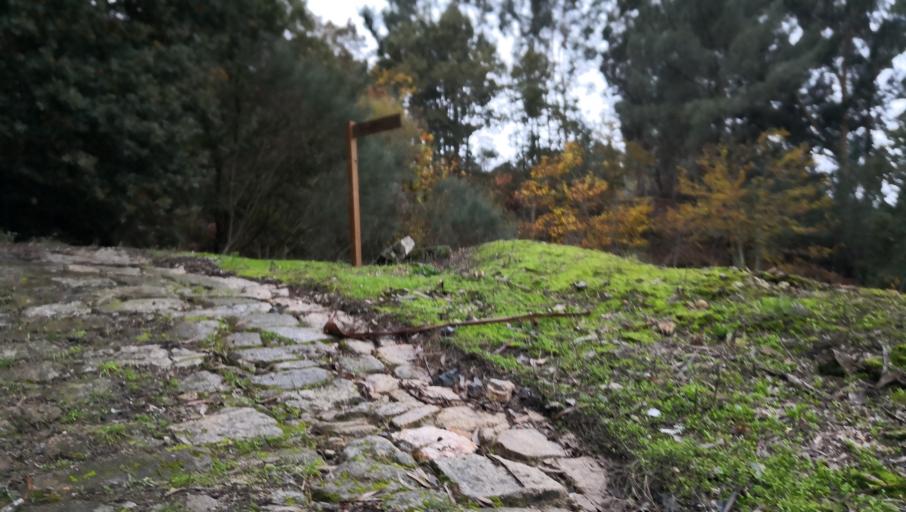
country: PT
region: Vila Real
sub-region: Vila Real
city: Vila Real
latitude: 41.2860
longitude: -7.7471
